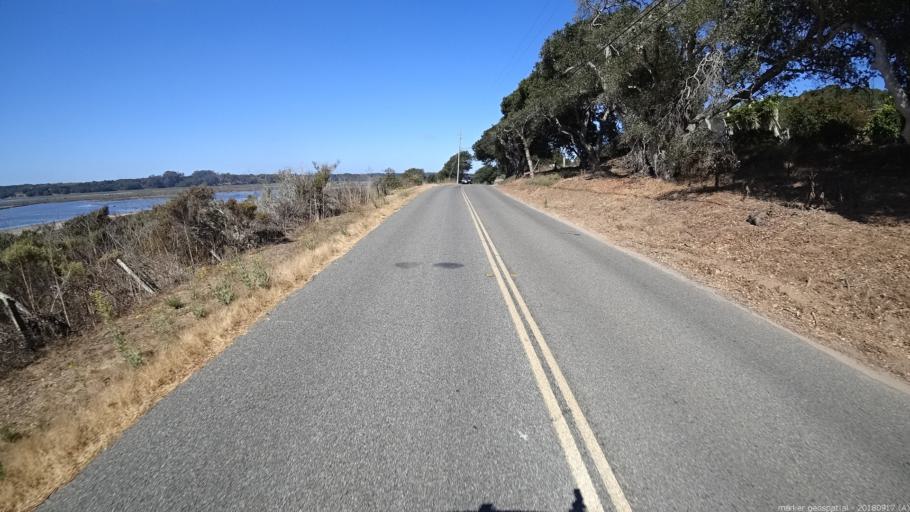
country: US
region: California
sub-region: Monterey County
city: Elkhorn
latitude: 36.8400
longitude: -121.7361
